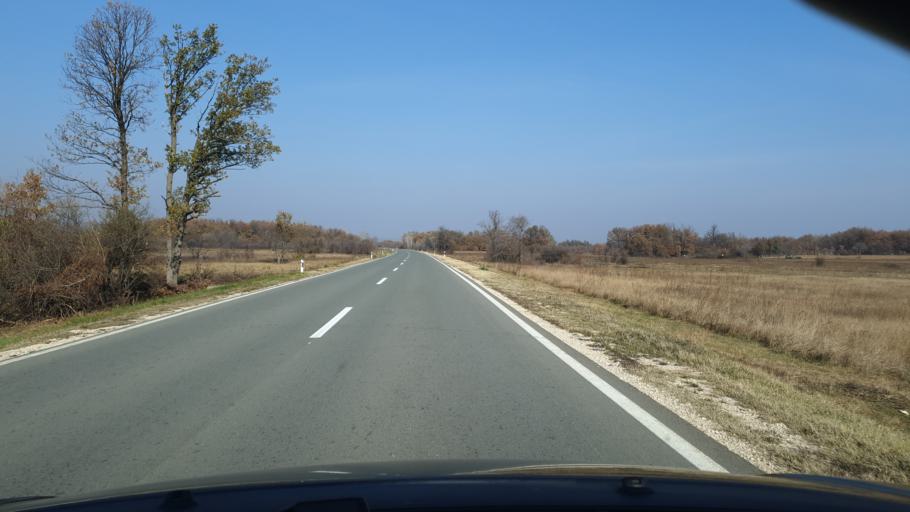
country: RS
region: Central Serbia
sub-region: Borski Okrug
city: Negotin
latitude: 44.1676
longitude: 22.3639
